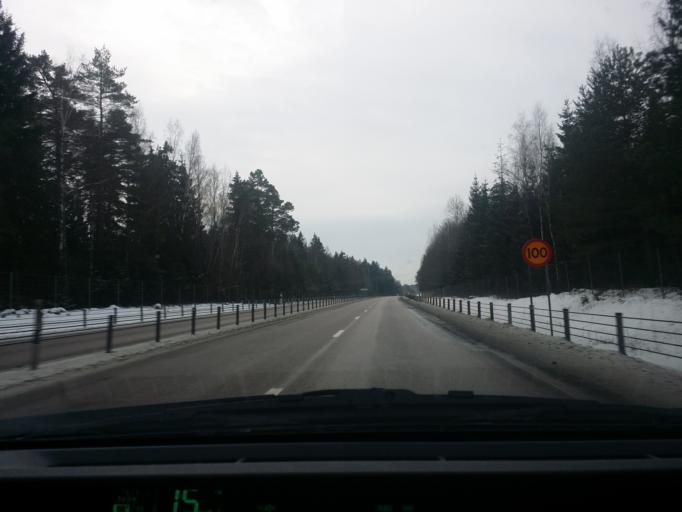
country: SE
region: Vaestra Goetaland
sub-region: Mariestads Kommun
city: Mariestad
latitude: 58.6451
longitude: 13.8207
